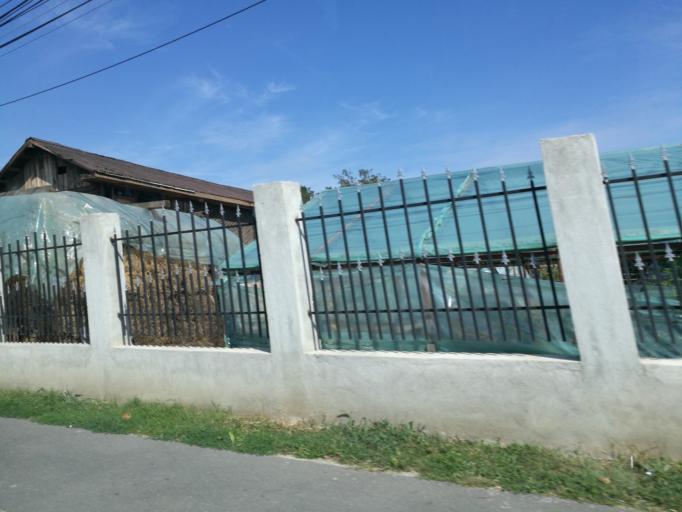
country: RO
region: Ilfov
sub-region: Comuna Otopeni
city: Otopeni
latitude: 44.5491
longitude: 26.0803
